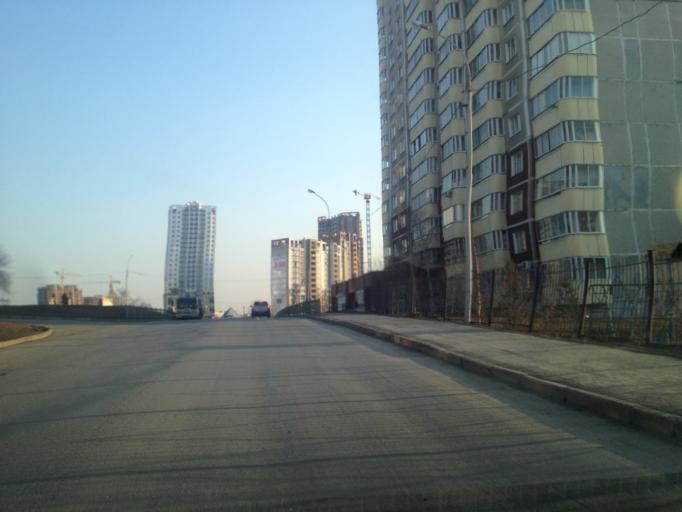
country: RU
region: Sverdlovsk
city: Sovkhoznyy
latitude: 56.8272
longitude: 60.5509
